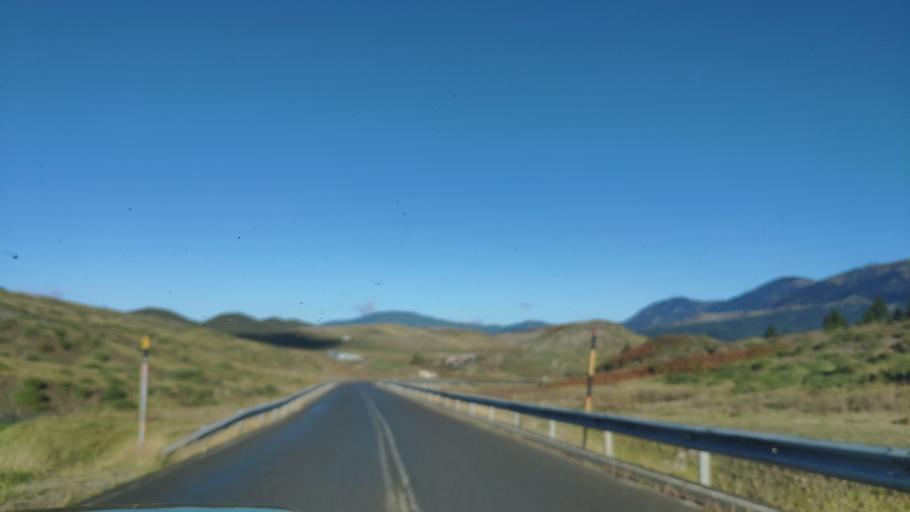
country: GR
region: Epirus
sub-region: Nomos Ioanninon
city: Metsovo
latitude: 39.8045
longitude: 21.1724
